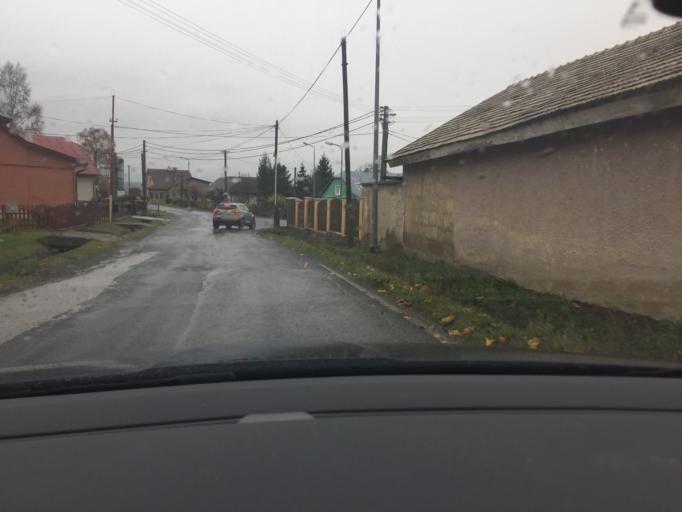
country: SK
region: Presovsky
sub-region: Okres Presov
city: Kezmarok
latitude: 49.1885
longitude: 20.3874
